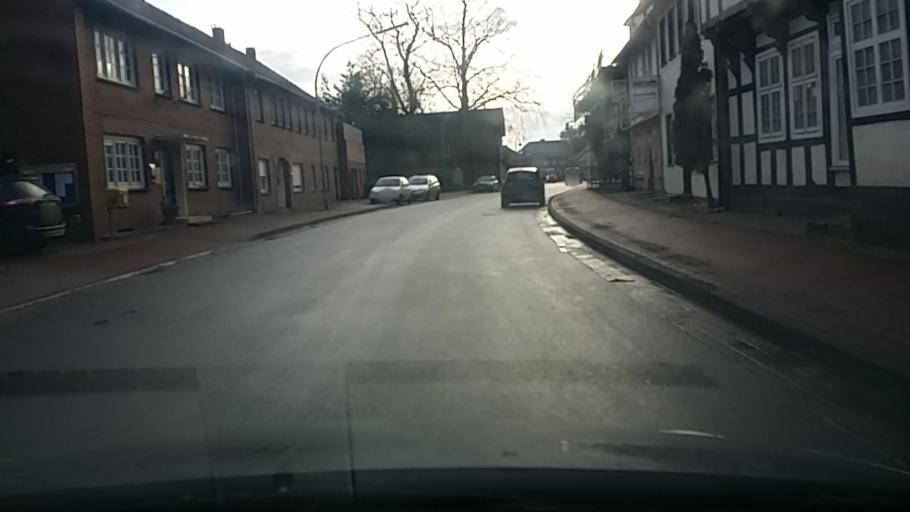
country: DE
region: Lower Saxony
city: Menslage
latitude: 52.6764
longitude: 7.8175
